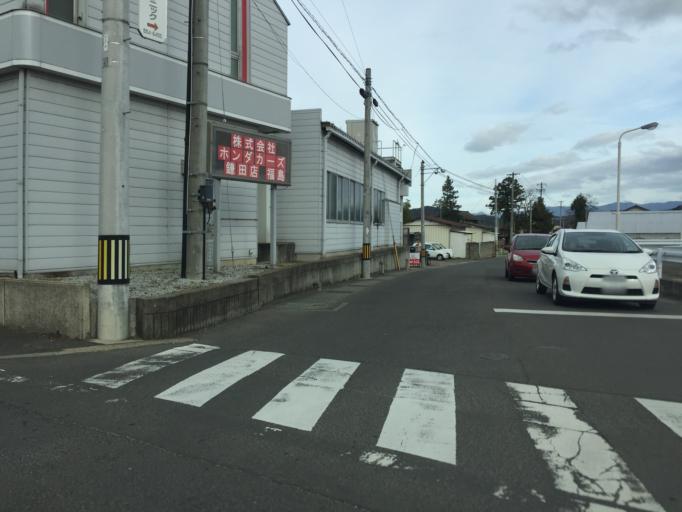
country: JP
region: Fukushima
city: Fukushima-shi
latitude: 37.7937
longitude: 140.4888
